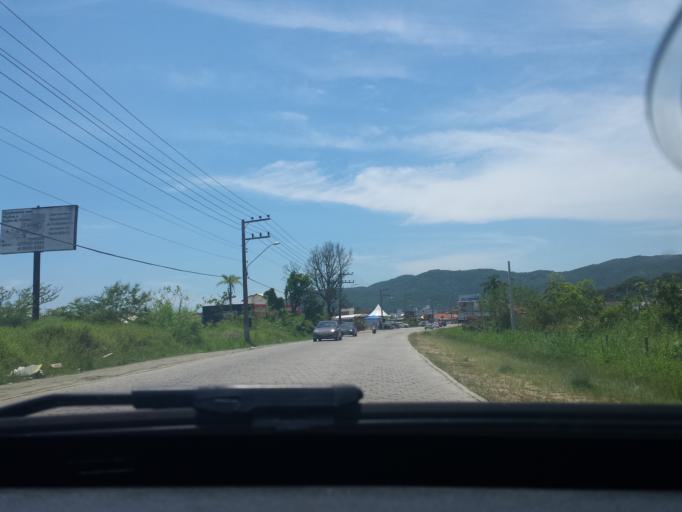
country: BR
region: Santa Catarina
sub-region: Porto Belo
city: Porto Belo
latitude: -27.1574
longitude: -48.5861
